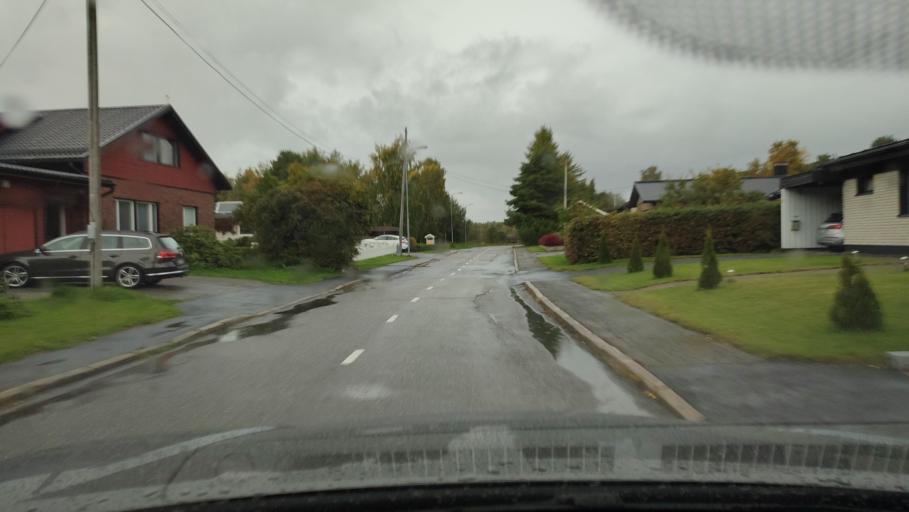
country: FI
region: Ostrobothnia
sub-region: Sydosterbotten
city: Kristinestad
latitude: 62.2822
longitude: 21.3746
